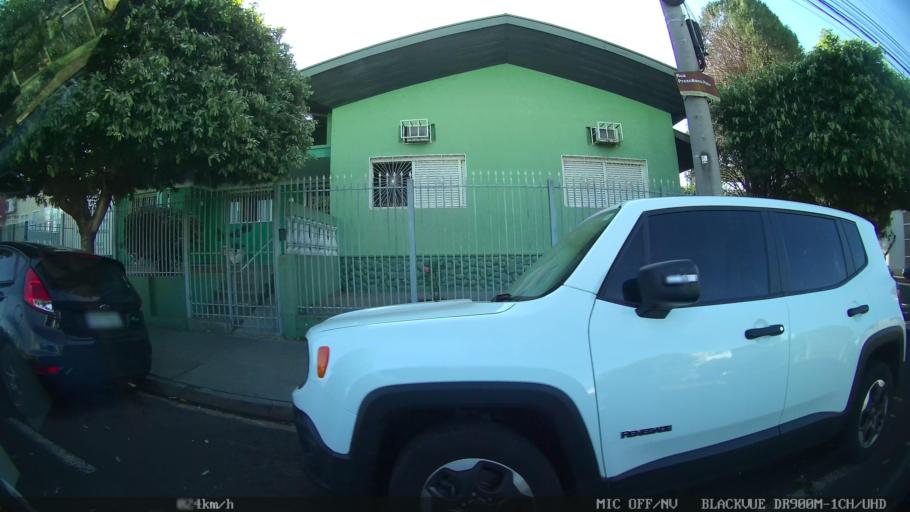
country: BR
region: Sao Paulo
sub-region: Sao Jose Do Rio Preto
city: Sao Jose do Rio Preto
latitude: -20.8165
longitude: -49.3957
